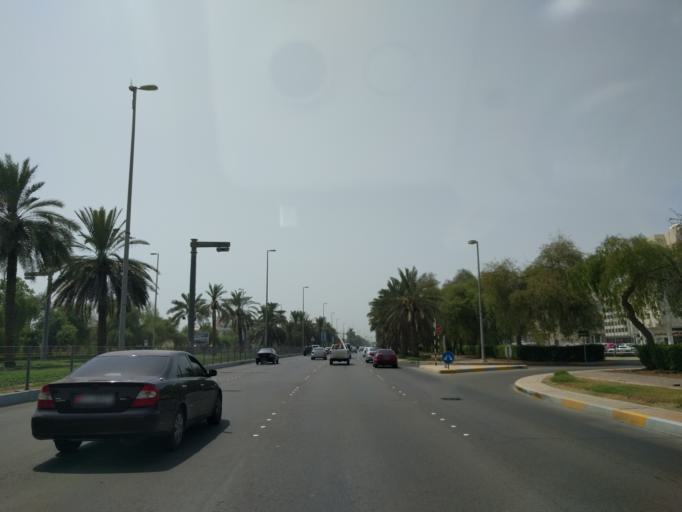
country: AE
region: Abu Dhabi
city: Abu Dhabi
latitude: 24.4433
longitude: 54.4045
